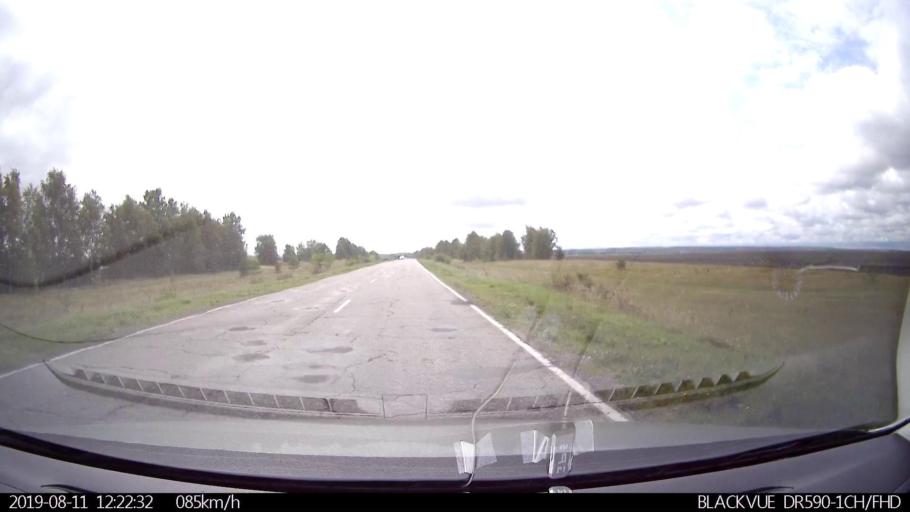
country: RU
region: Ulyanovsk
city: Ignatovka
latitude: 53.9065
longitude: 47.9534
